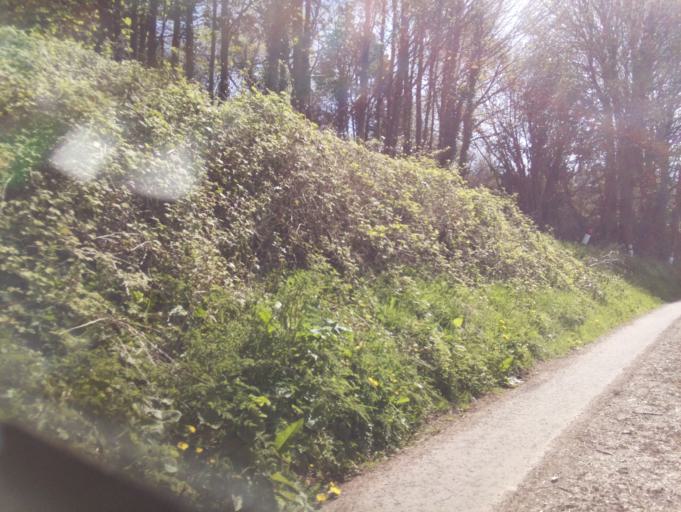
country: GB
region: Wales
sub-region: Monmouthshire
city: Llangwm
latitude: 51.6835
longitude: -2.8116
